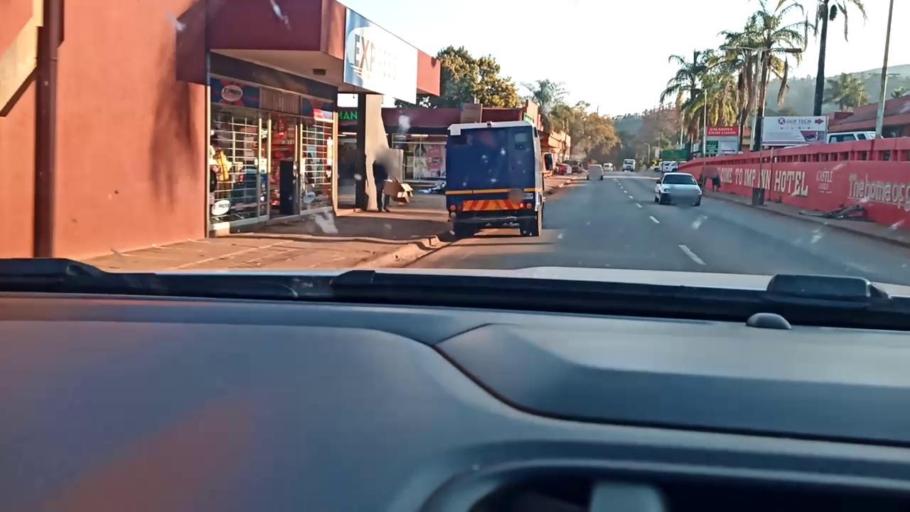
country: ZA
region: Limpopo
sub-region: Mopani District Municipality
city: Duiwelskloof
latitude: -23.6971
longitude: 30.1393
